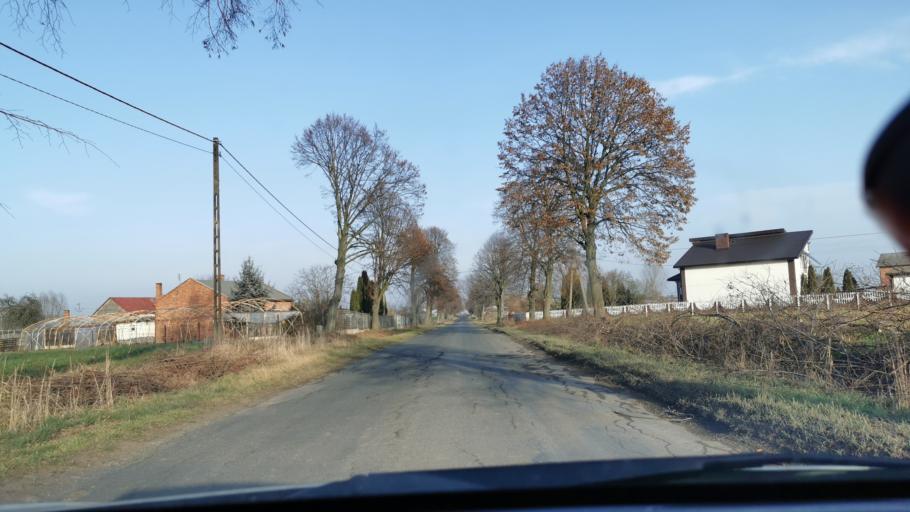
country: PL
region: Greater Poland Voivodeship
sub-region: Powiat kaliski
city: Opatowek
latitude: 51.6806
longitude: 18.3074
